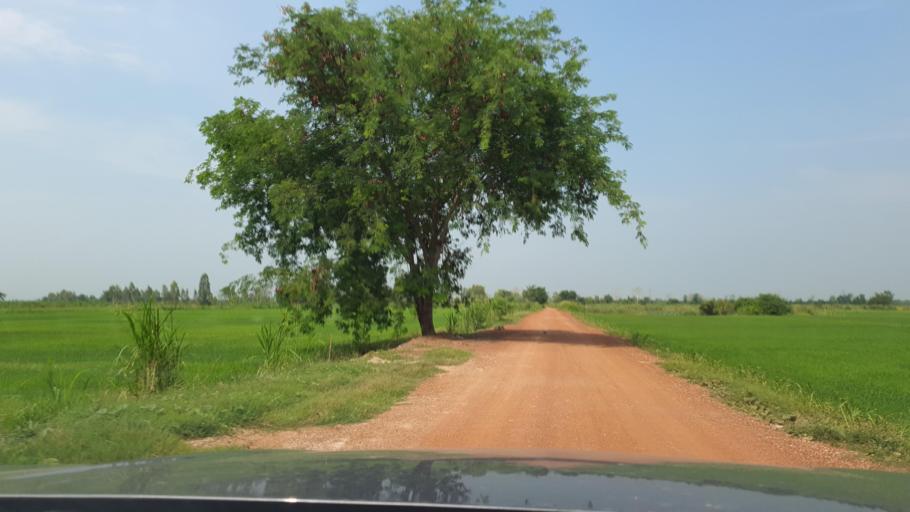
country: TH
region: Phitsanulok
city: Bang Rakam
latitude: 16.8012
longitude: 100.1109
